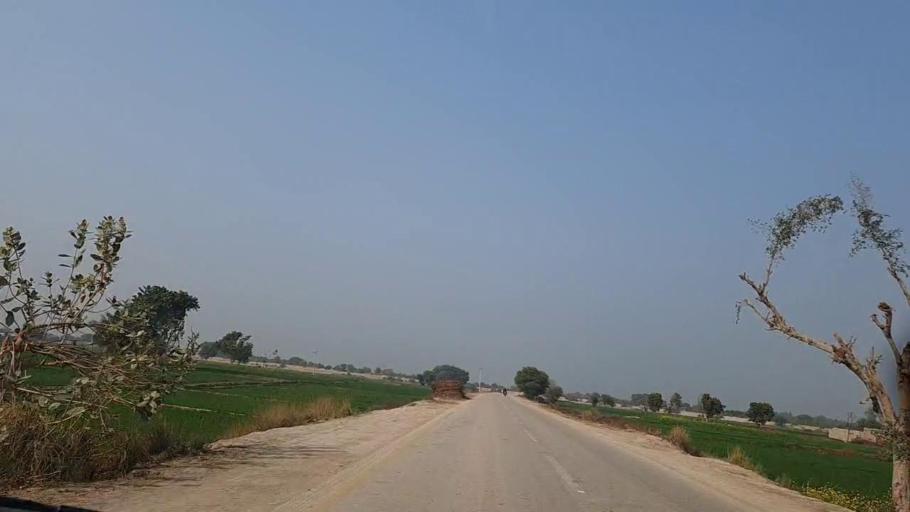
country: PK
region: Sindh
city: Sann
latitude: 26.1721
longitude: 68.1072
